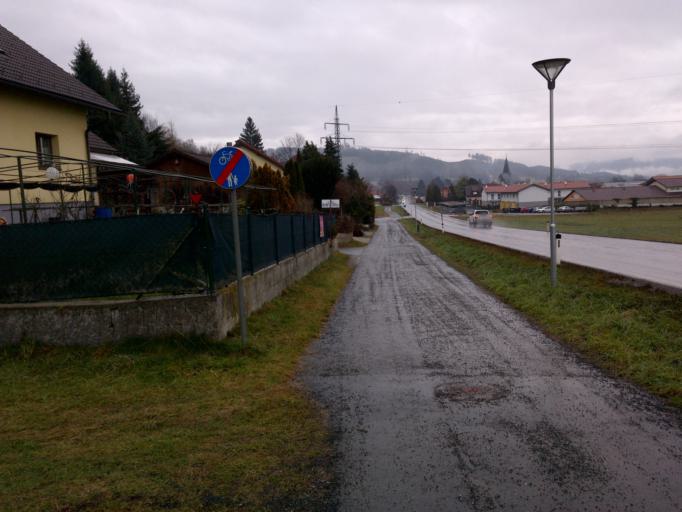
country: AT
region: Styria
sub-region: Politischer Bezirk Murtal
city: Kobenz
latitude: 47.2439
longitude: 14.8385
